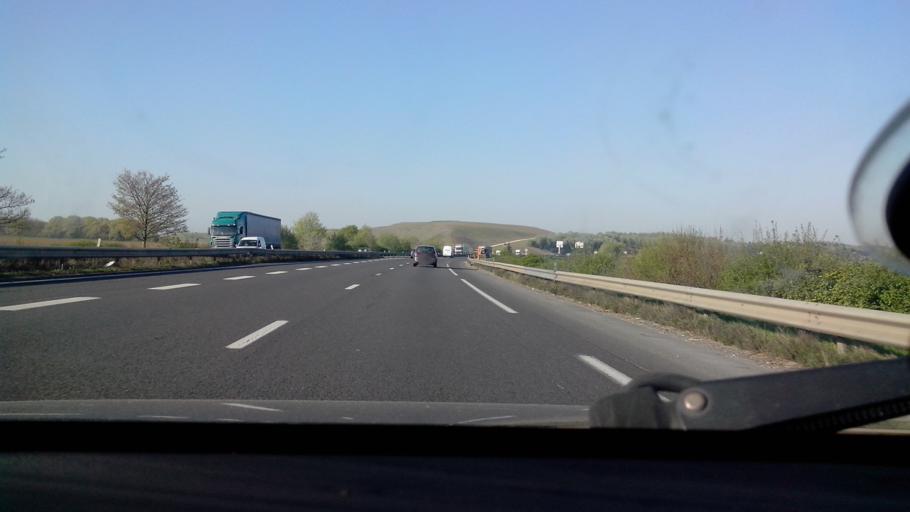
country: FR
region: Ile-de-France
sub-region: Departement de Seine-et-Marne
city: Moissy-Cramayel
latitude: 48.6502
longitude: 2.6107
